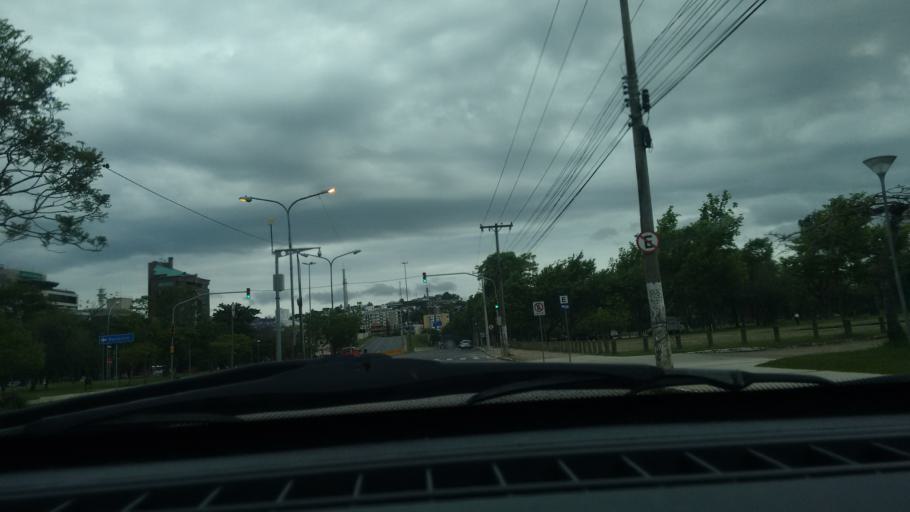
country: BR
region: Rio Grande do Sul
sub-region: Porto Alegre
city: Porto Alegre
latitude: -30.0561
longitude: -51.2304
